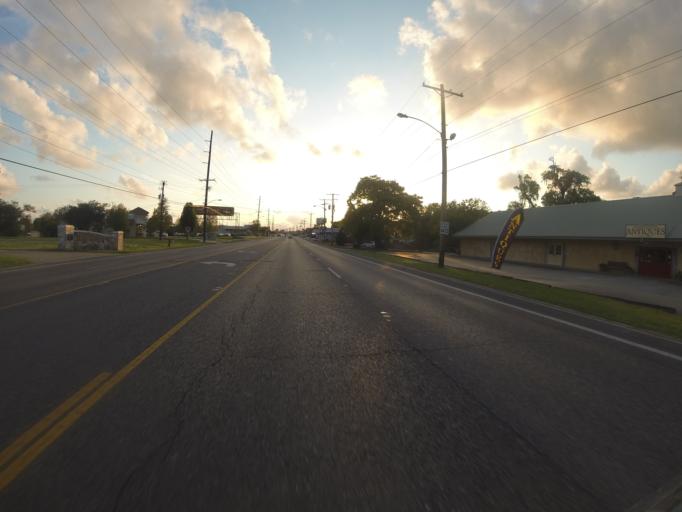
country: US
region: Louisiana
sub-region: Lafayette Parish
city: Lafayette
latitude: 30.2045
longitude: -92.0452
